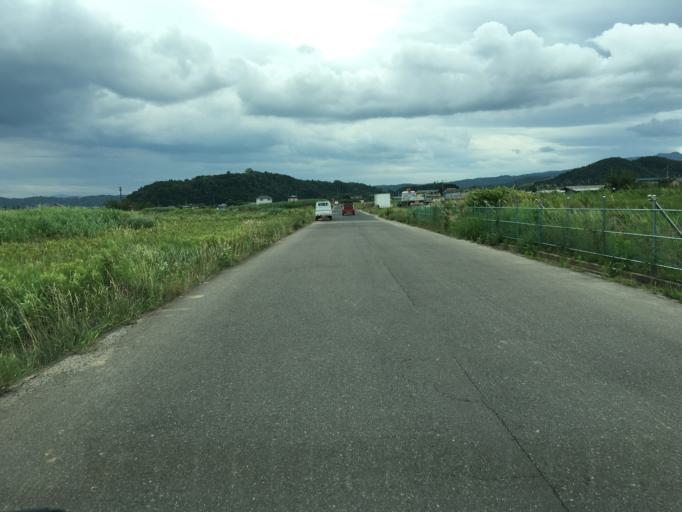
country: JP
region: Fukushima
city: Fukushima-shi
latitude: 37.7371
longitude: 140.4299
